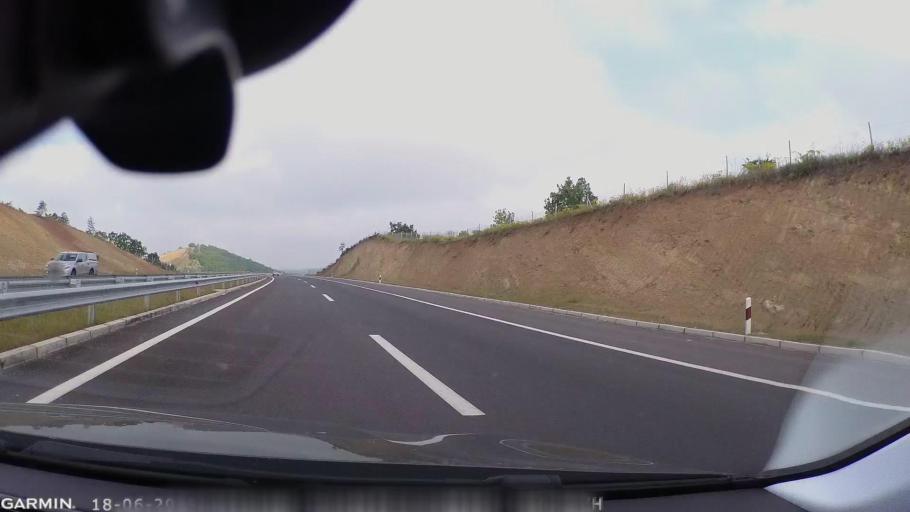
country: MK
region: Sveti Nikole
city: Gorobinci
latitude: 41.9206
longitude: 21.8658
